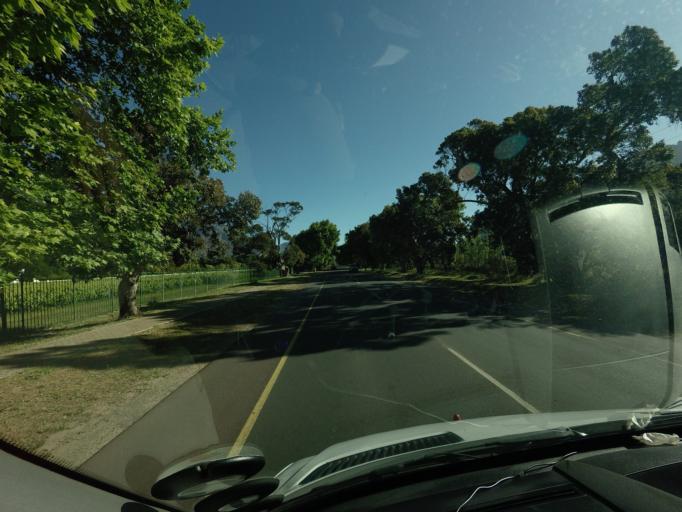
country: ZA
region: Western Cape
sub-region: Cape Winelands District Municipality
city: Stellenbosch
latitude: -33.8721
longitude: 18.9748
